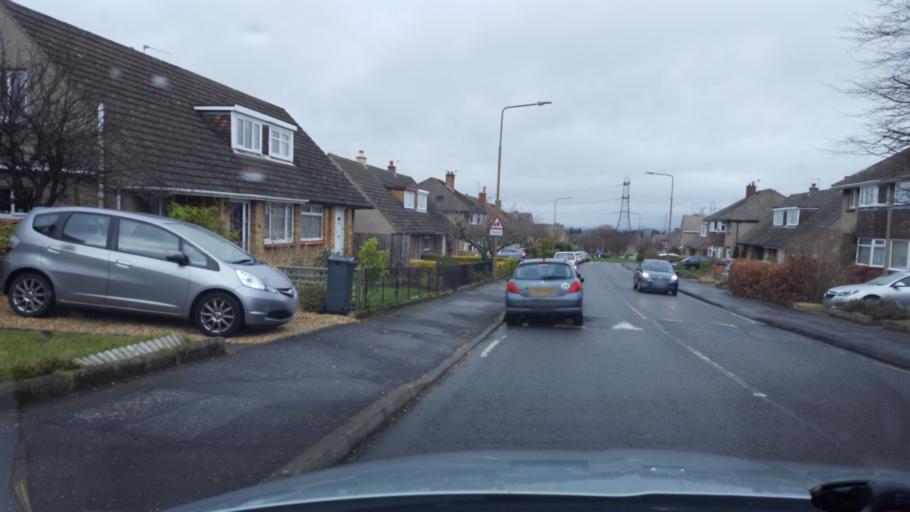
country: GB
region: Scotland
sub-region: Edinburgh
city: Currie
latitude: 55.8985
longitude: -3.3090
